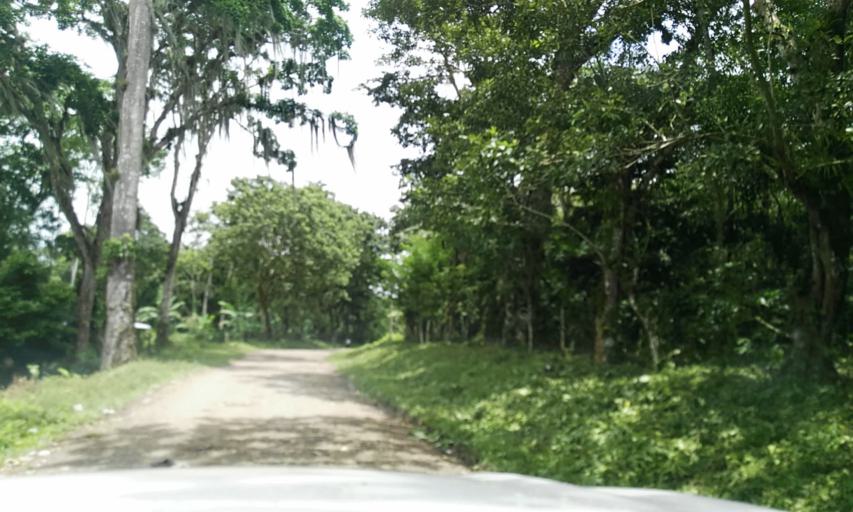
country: NI
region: Matagalpa
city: San Ramon
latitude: 12.9962
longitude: -85.8668
